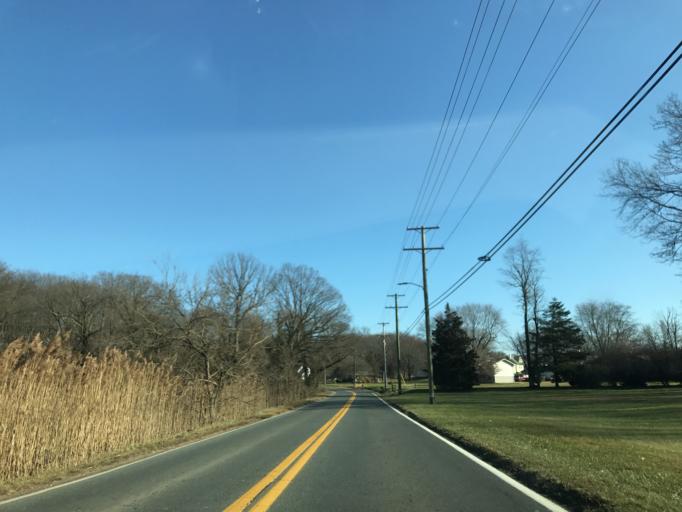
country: US
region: Maryland
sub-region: Baltimore County
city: Bowleys Quarters
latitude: 39.3628
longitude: -76.3920
